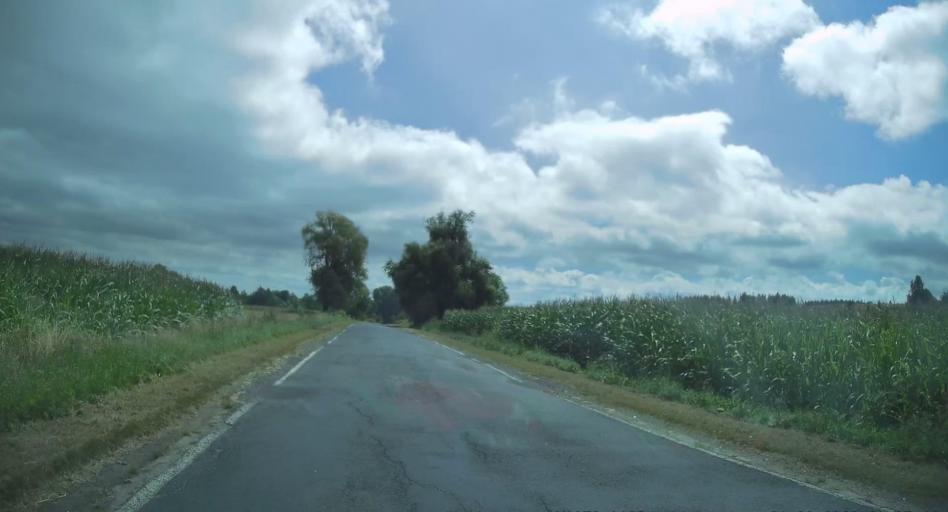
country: PL
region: Swietokrzyskie
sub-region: Powiat sandomierski
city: Klimontow
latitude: 50.6826
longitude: 21.3880
